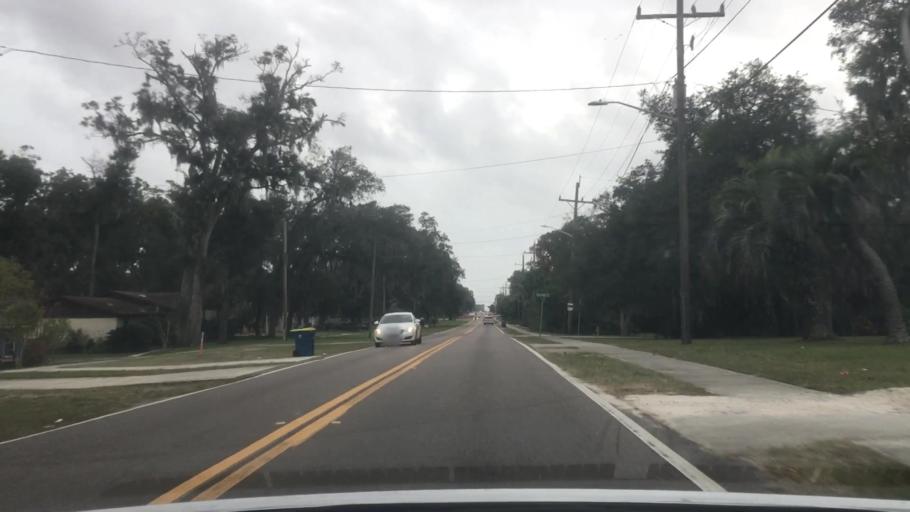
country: US
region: Florida
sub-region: Duval County
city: Atlantic Beach
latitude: 30.3531
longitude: -81.5238
